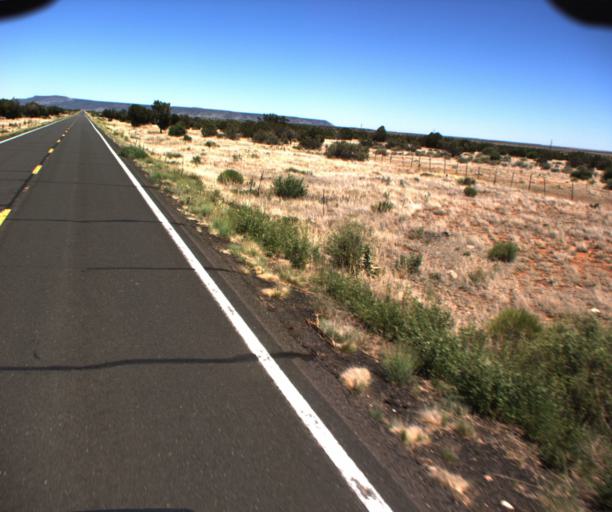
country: US
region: Arizona
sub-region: Coconino County
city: LeChee
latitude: 34.7495
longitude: -111.0406
